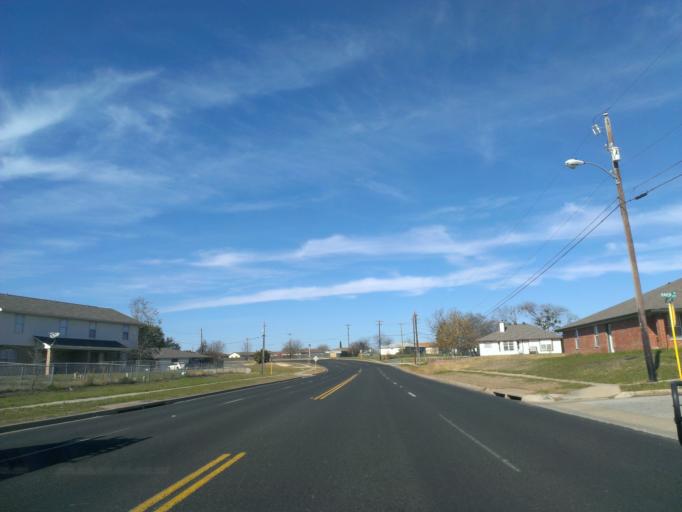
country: US
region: Texas
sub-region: Bell County
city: Killeen
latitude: 31.1310
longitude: -97.6921
